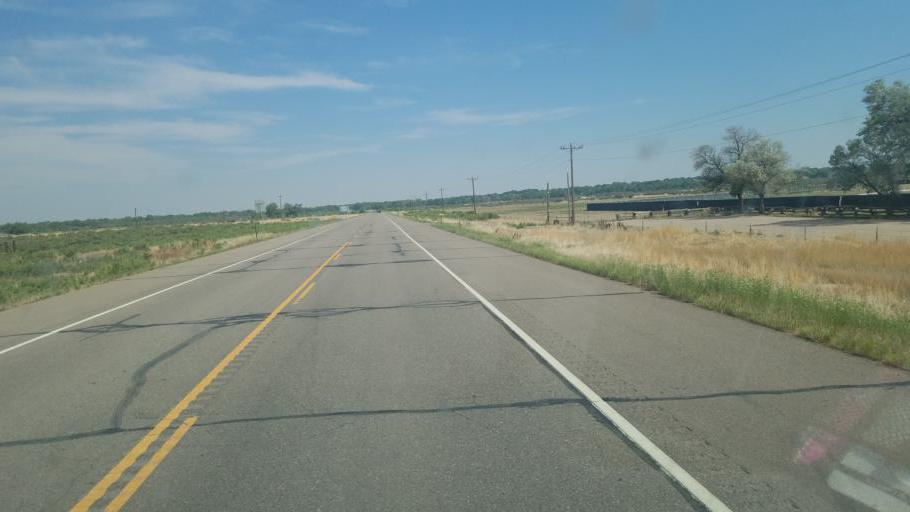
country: US
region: Colorado
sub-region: Pueblo County
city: Pueblo
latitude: 38.2566
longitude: -104.3611
